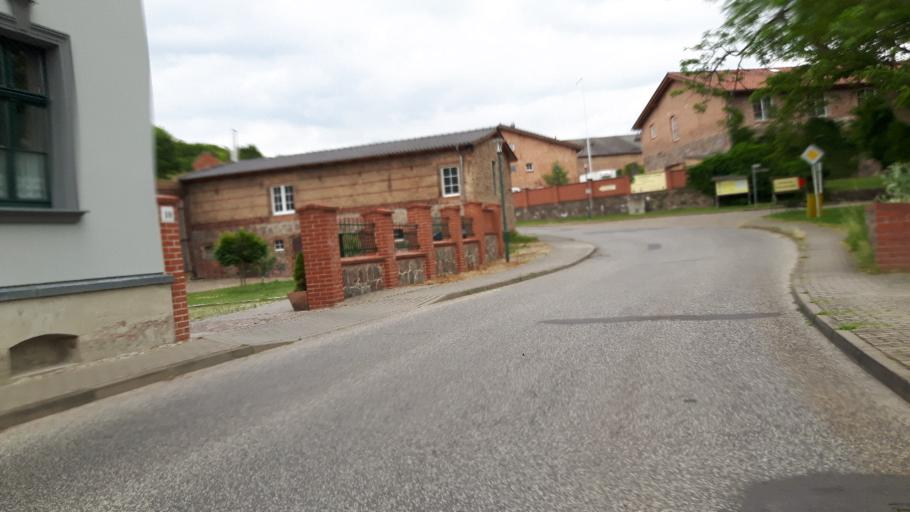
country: DE
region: Brandenburg
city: Liepe
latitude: 52.8624
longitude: 13.9709
